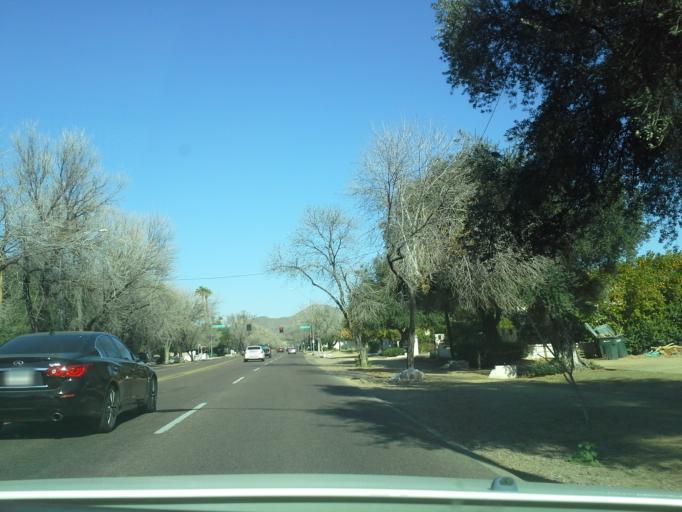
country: US
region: Arizona
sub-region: Maricopa County
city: Phoenix
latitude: 33.5512
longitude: -112.0738
